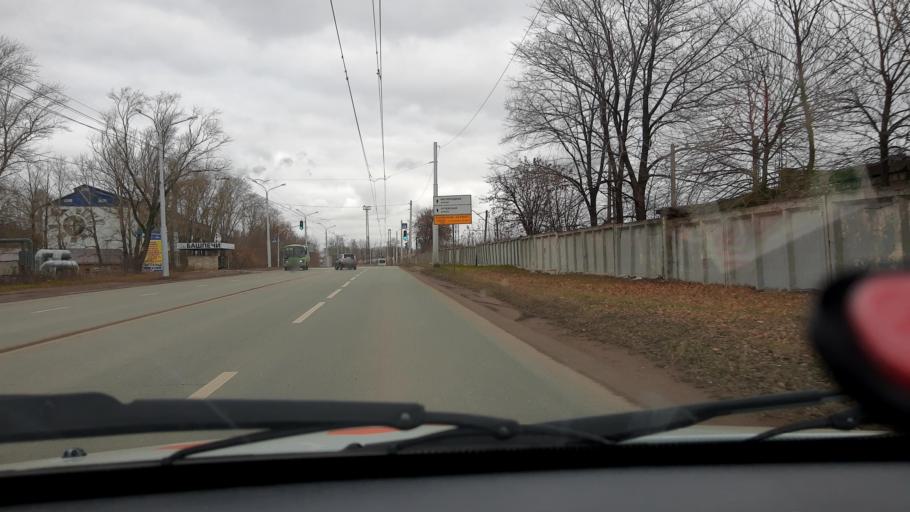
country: RU
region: Bashkortostan
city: Ufa
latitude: 54.8279
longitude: 56.0859
